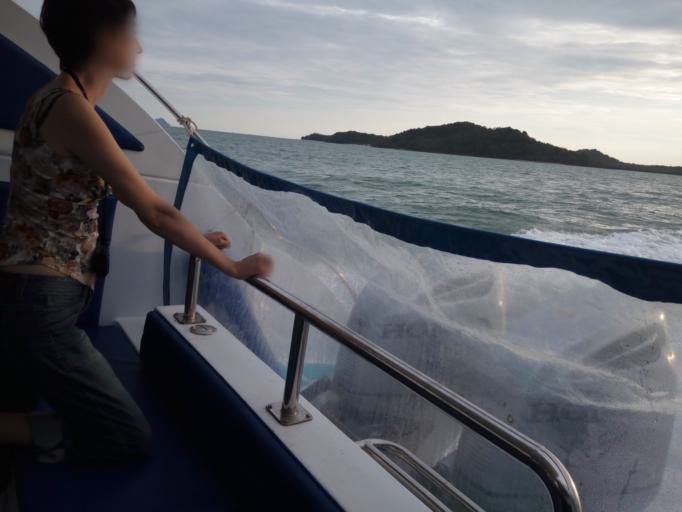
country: TH
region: Phangnga
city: Ko Yao
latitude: 8.0722
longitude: 98.4693
